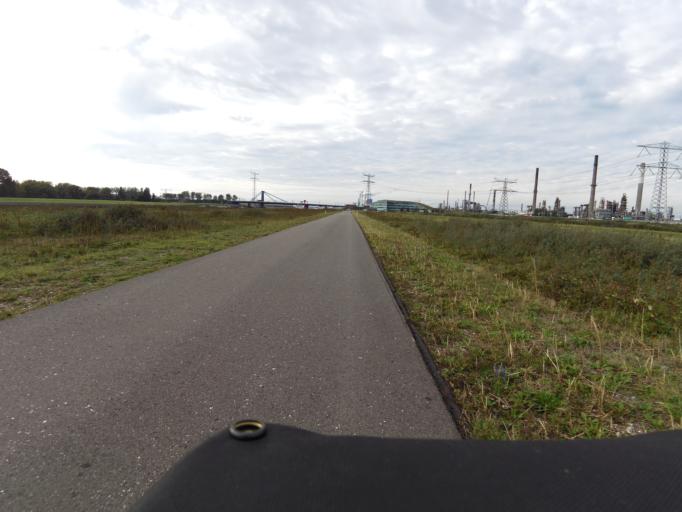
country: NL
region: South Holland
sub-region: Gemeente Rotterdam
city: Hoek van Holland
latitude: 51.9372
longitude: 4.1171
